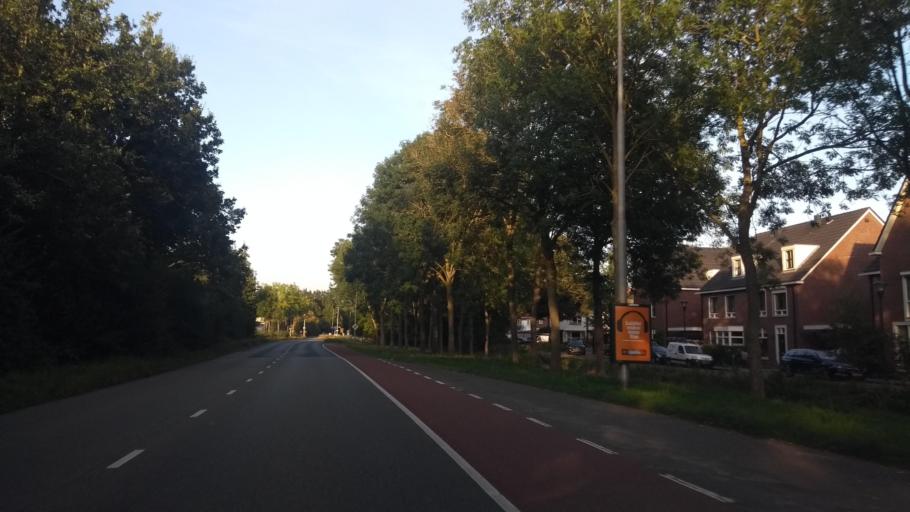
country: NL
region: Gelderland
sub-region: Gemeente Zutphen
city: Zutphen
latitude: 52.1438
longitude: 6.2073
